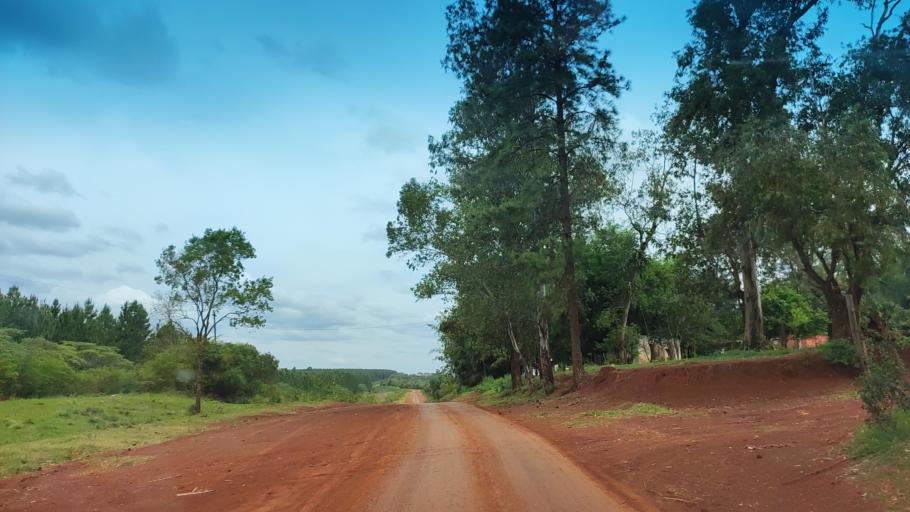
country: AR
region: Misiones
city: Garupa
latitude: -27.4939
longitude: -55.9708
